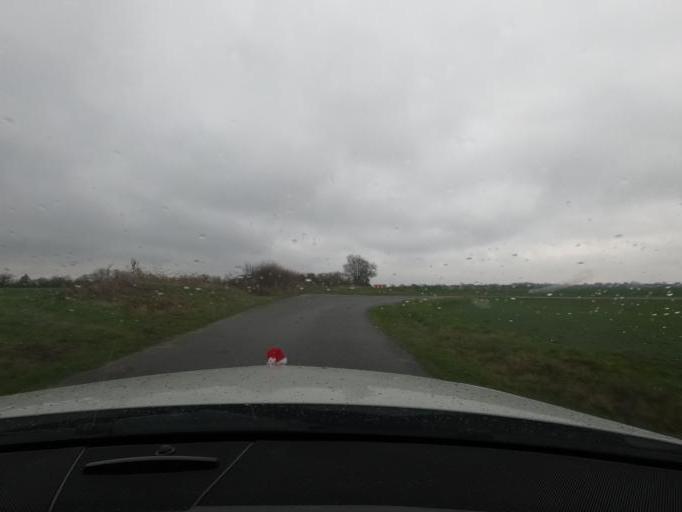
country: DK
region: South Denmark
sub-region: Haderslev Kommune
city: Starup
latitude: 55.1983
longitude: 9.6427
